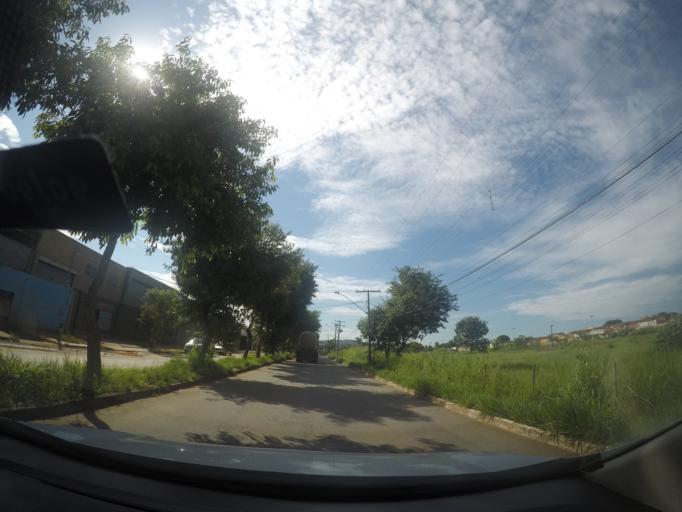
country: BR
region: Goias
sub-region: Goiania
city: Goiania
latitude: -16.6614
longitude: -49.2089
